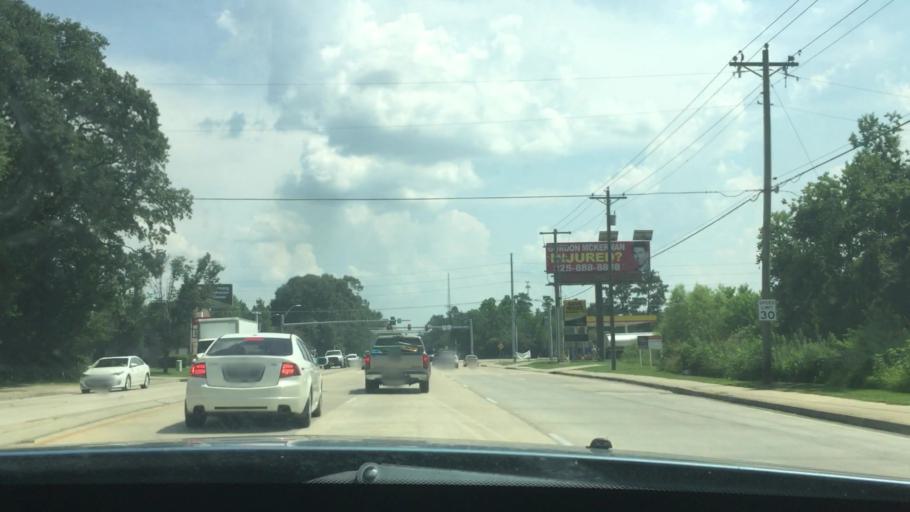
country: US
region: Louisiana
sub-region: East Baton Rouge Parish
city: Shenandoah
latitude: 30.4268
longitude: -91.0076
